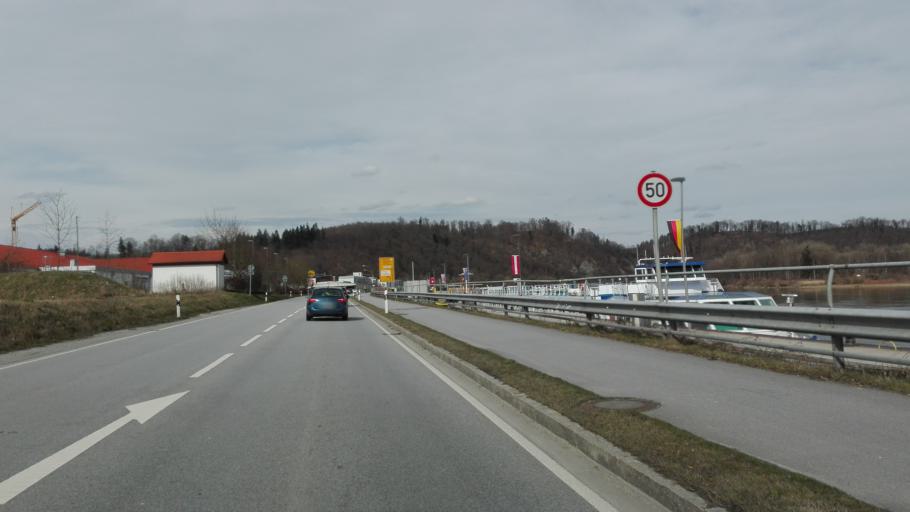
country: DE
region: Bavaria
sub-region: Lower Bavaria
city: Salzweg
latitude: 48.5829
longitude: 13.5002
